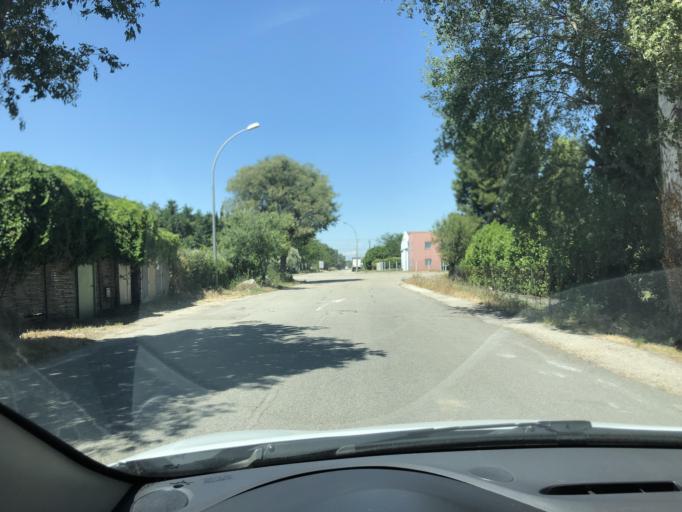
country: FR
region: Provence-Alpes-Cote d'Azur
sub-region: Departement des Bouches-du-Rhone
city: Chateaurenard
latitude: 43.8963
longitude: 4.8750
